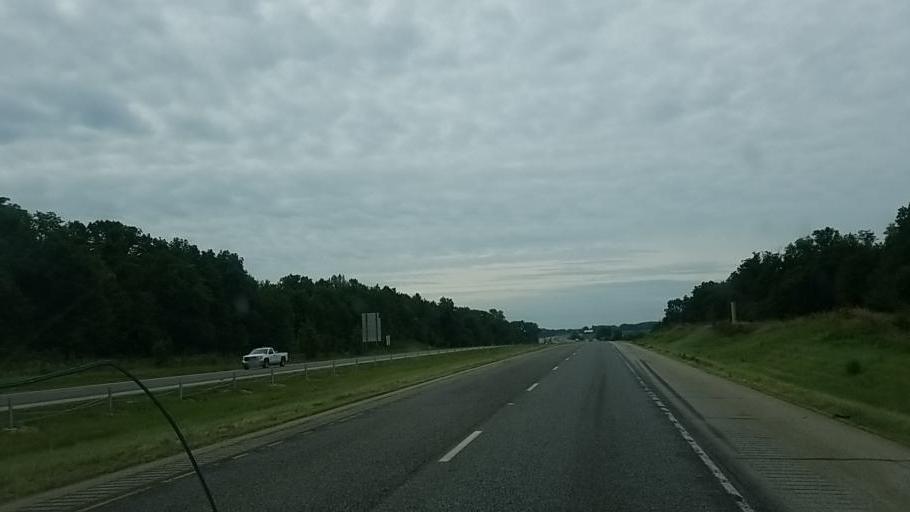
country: US
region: Indiana
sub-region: DeKalb County
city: Waterloo
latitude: 41.5100
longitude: -85.0555
